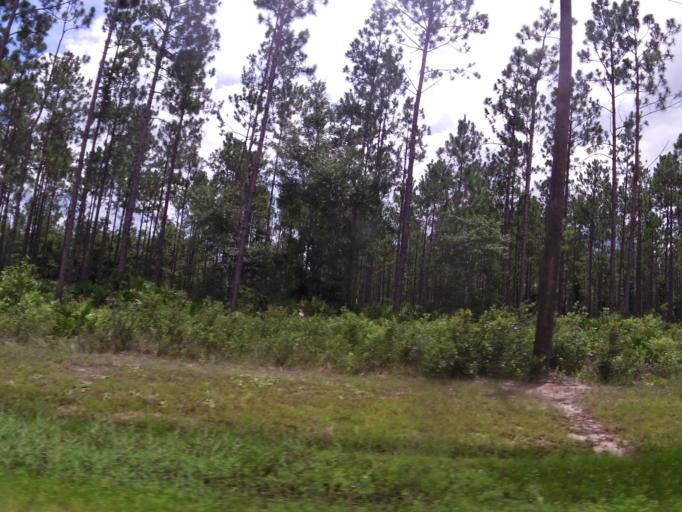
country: US
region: Florida
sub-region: Flagler County
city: Palm Coast
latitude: 29.6576
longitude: -81.3056
